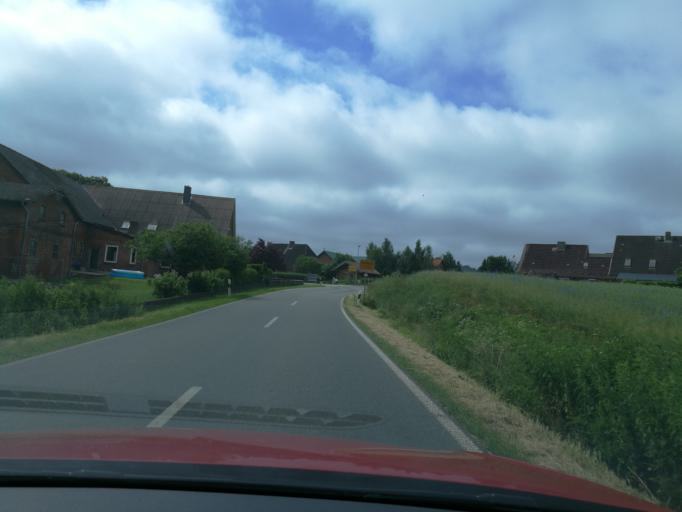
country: DE
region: Schleswig-Holstein
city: Lasbek
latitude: 53.7472
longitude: 10.3792
